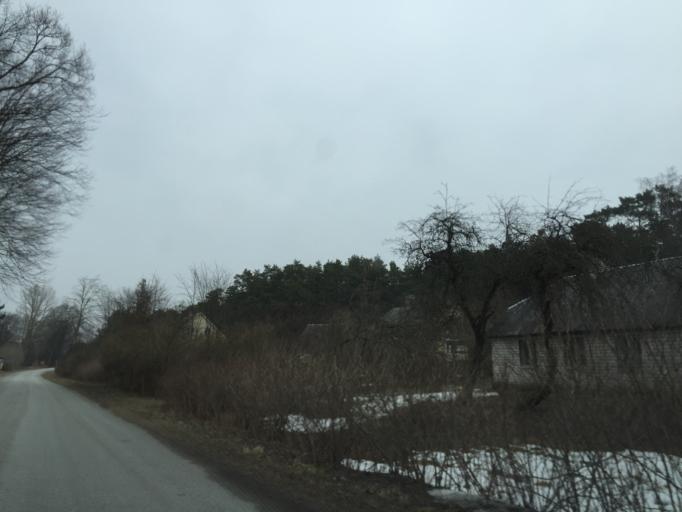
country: LV
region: Salacgrivas
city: Ainazi
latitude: 58.0337
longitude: 24.4609
